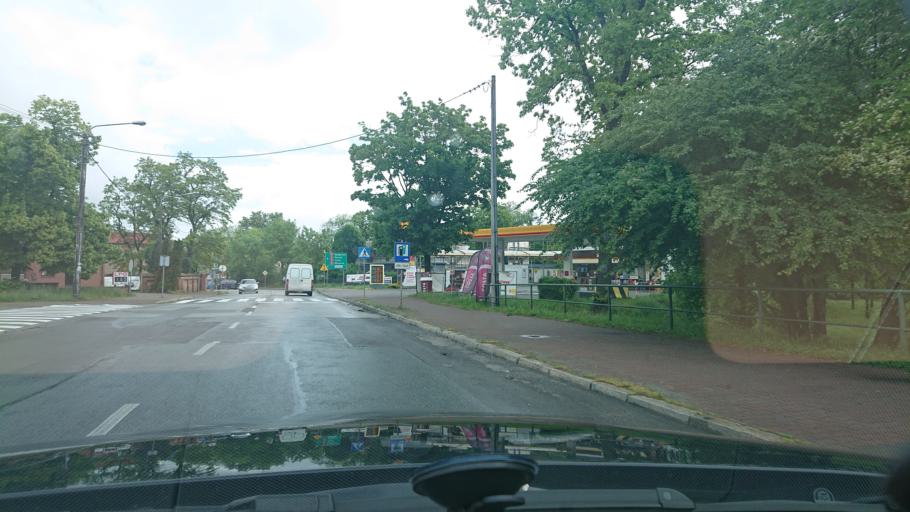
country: PL
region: Greater Poland Voivodeship
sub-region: Powiat gnieznienski
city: Gniezno
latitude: 52.5367
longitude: 17.6086
